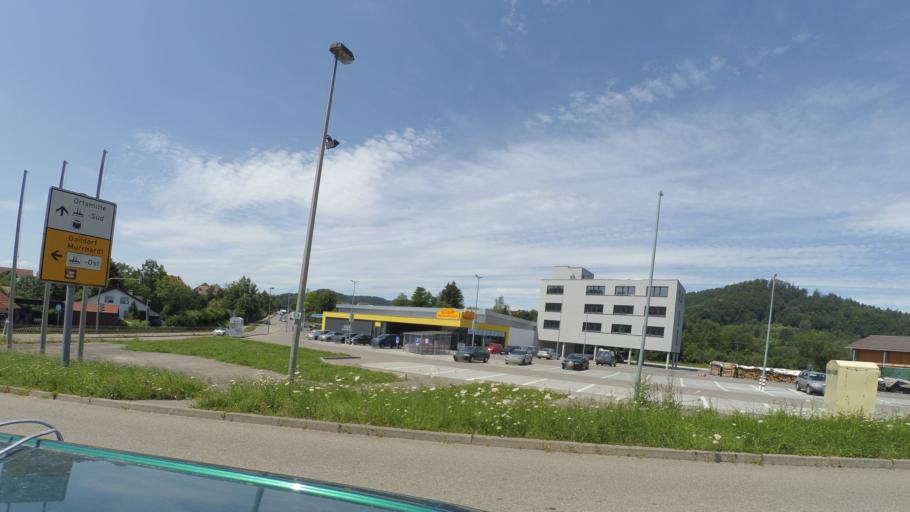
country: DE
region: Baden-Wuerttemberg
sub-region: Regierungsbezirk Stuttgart
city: Sulzbach an der Murr
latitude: 49.0051
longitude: 9.5036
